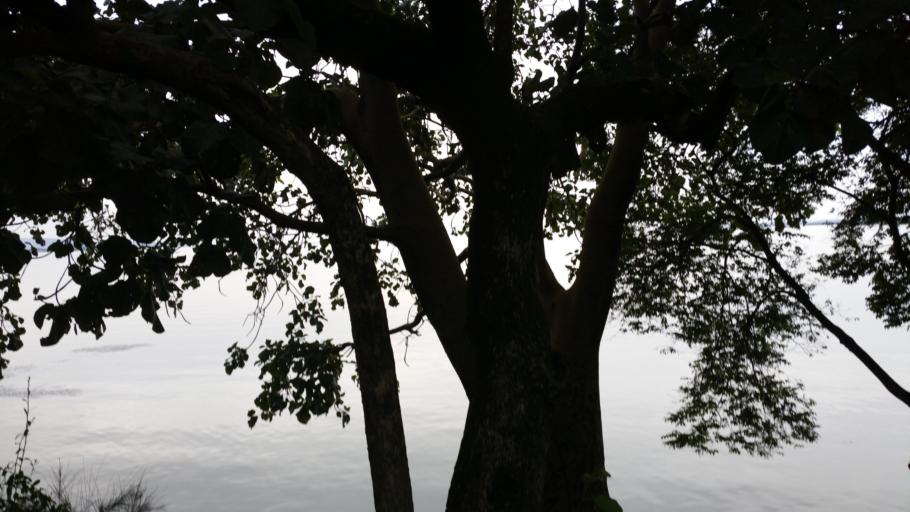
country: ET
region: Amhara
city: Bahir Dar
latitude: 11.5985
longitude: 37.3853
